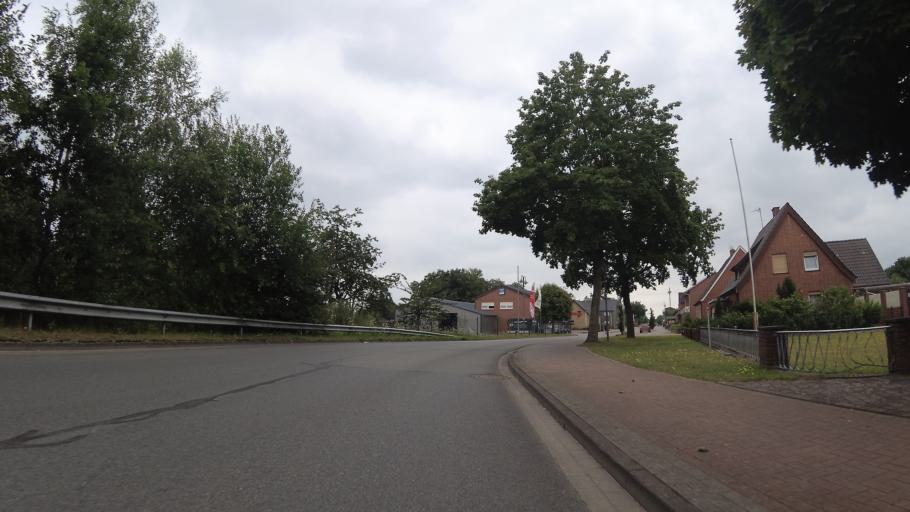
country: DE
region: Lower Saxony
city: Lathen
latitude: 52.8679
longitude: 7.3228
